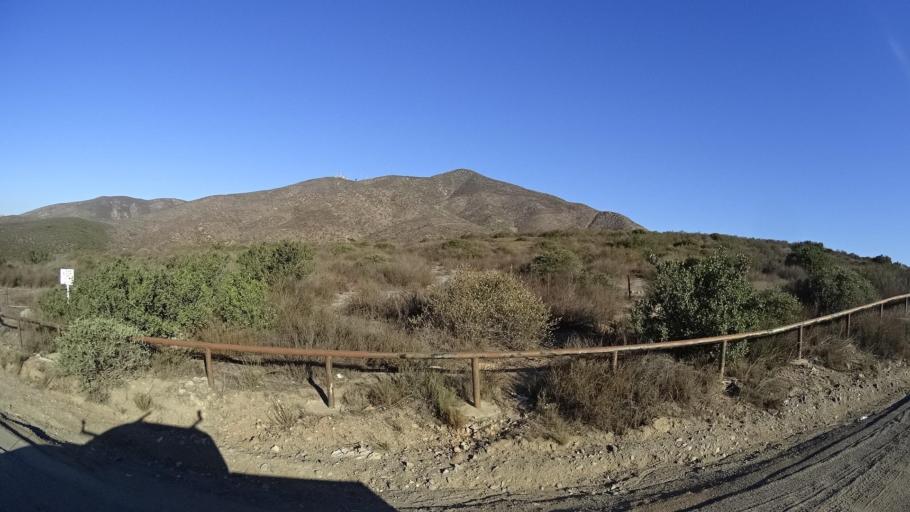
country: US
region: California
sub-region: San Diego County
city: Jamul
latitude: 32.6808
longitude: -116.9149
